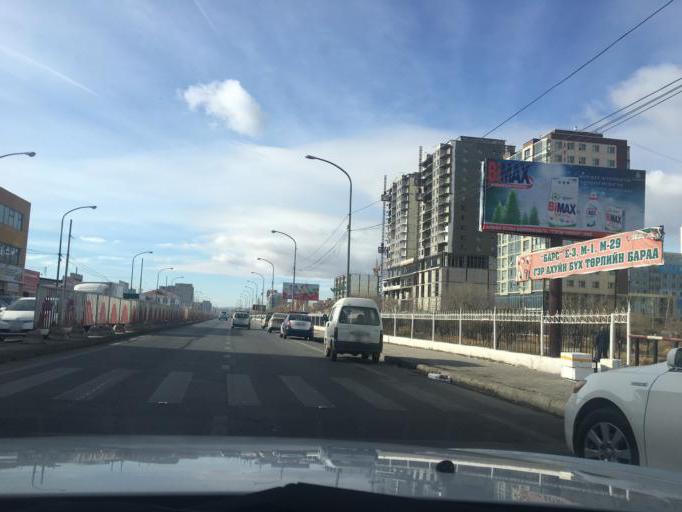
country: MN
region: Ulaanbaatar
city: Ulaanbaatar
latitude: 47.9091
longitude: 106.8909
